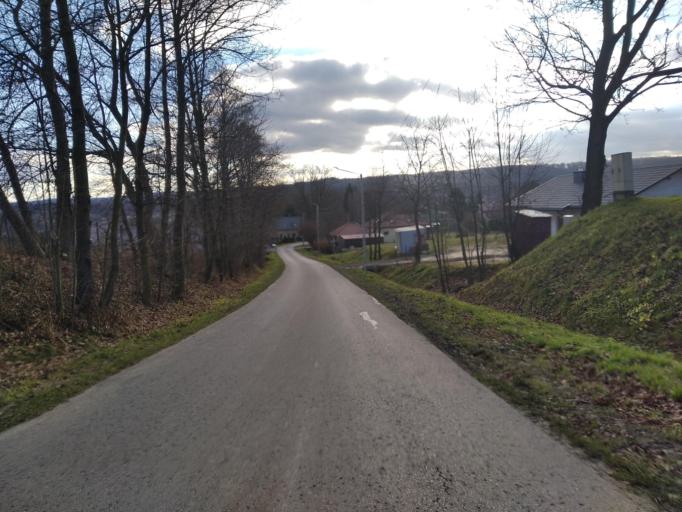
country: PL
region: Subcarpathian Voivodeship
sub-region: Powiat strzyzowski
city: Babica
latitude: 49.9365
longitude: 21.8616
